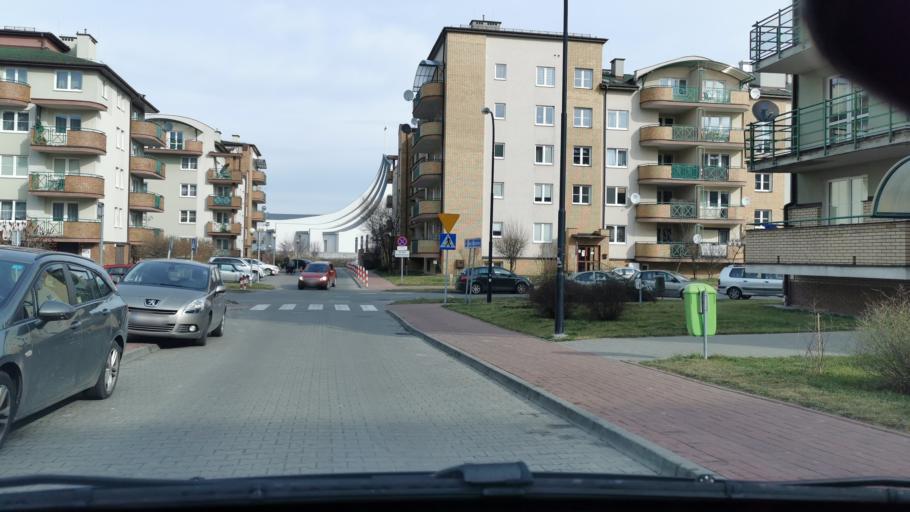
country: PL
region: Lublin Voivodeship
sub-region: Powiat lubelski
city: Lublin
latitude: 51.1999
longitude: 22.5459
